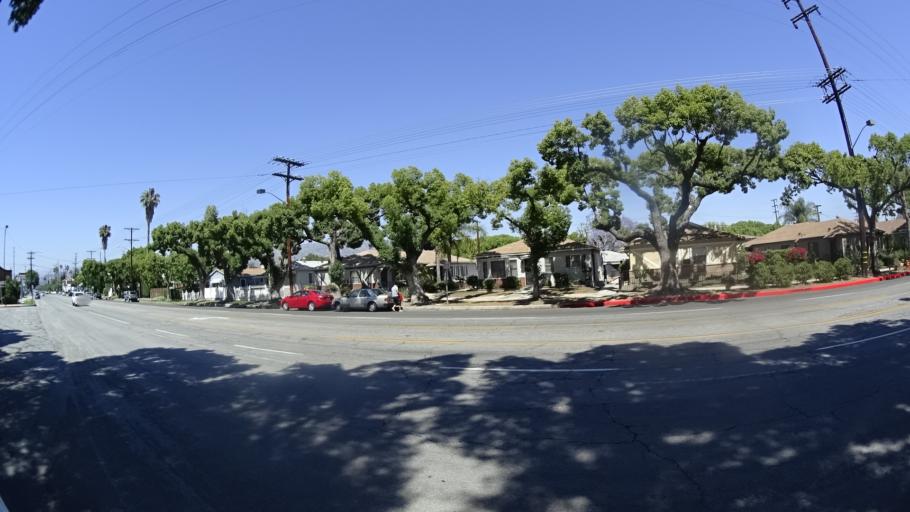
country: US
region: California
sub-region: Los Angeles County
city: North Hollywood
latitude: 34.1730
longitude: -118.3494
